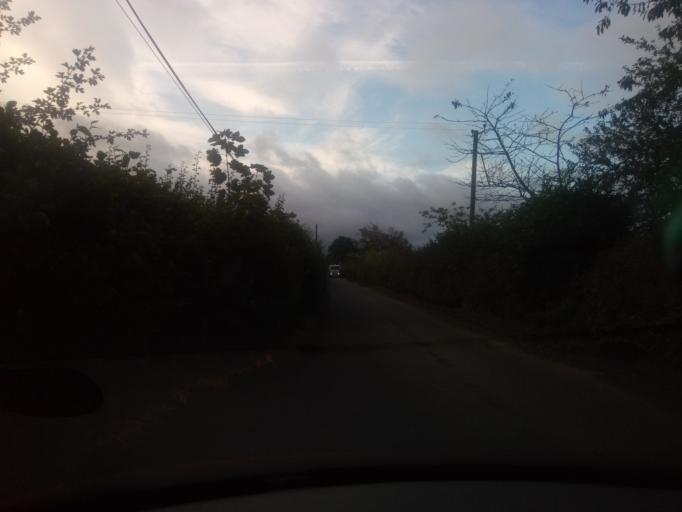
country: GB
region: Scotland
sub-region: The Scottish Borders
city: Jedburgh
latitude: 55.3829
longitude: -2.6426
